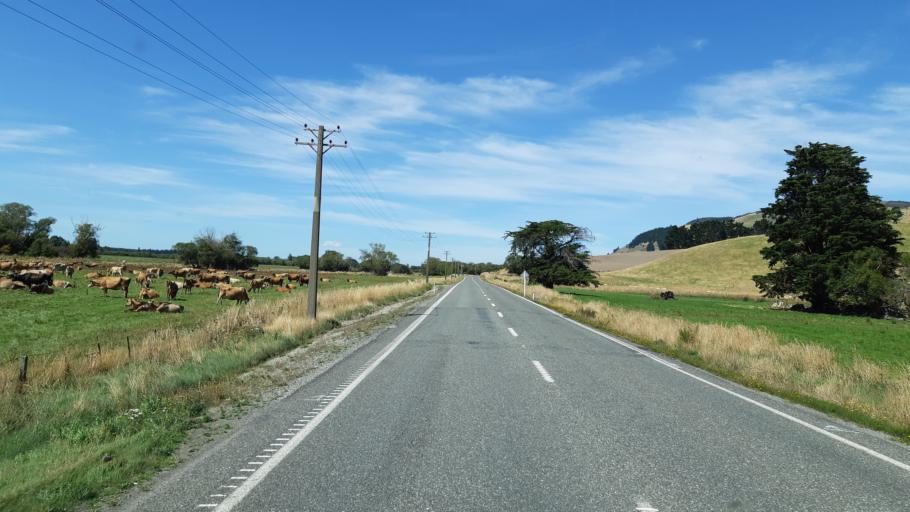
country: NZ
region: Southland
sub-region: Gore District
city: Gore
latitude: -46.0036
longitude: 168.8283
